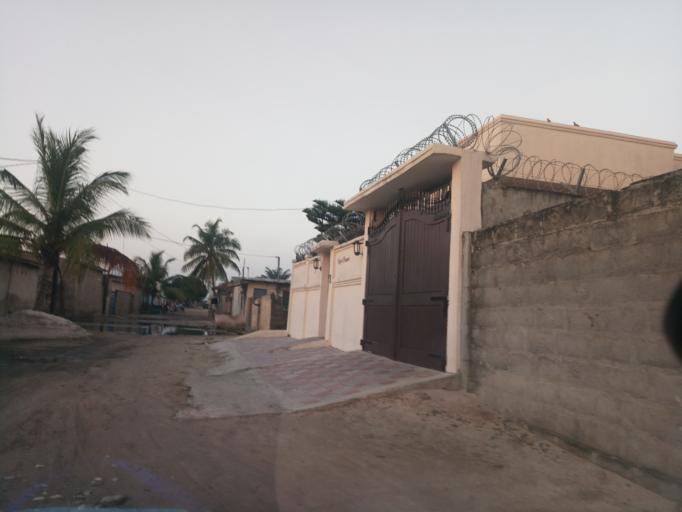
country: BJ
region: Atlantique
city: Hevie
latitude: 6.3892
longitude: 2.2879
